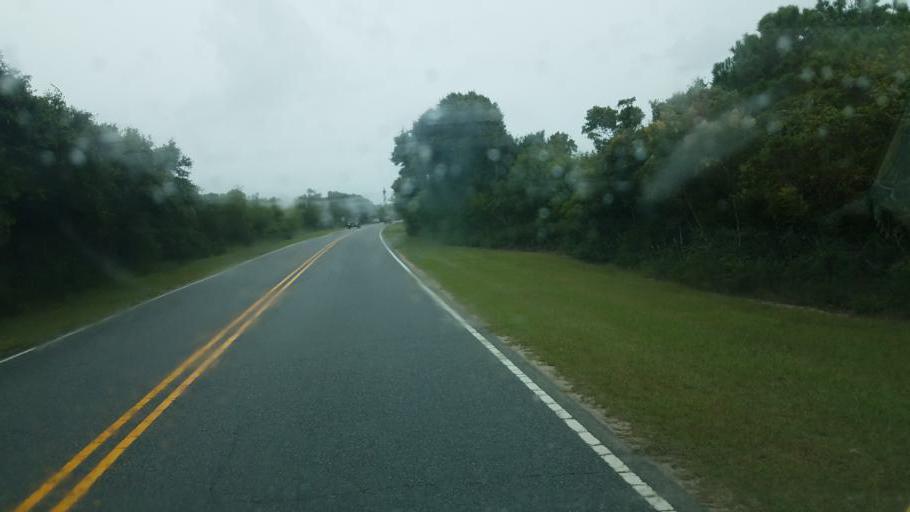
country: US
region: North Carolina
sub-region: Dare County
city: Buxton
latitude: 35.2622
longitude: -75.5253
